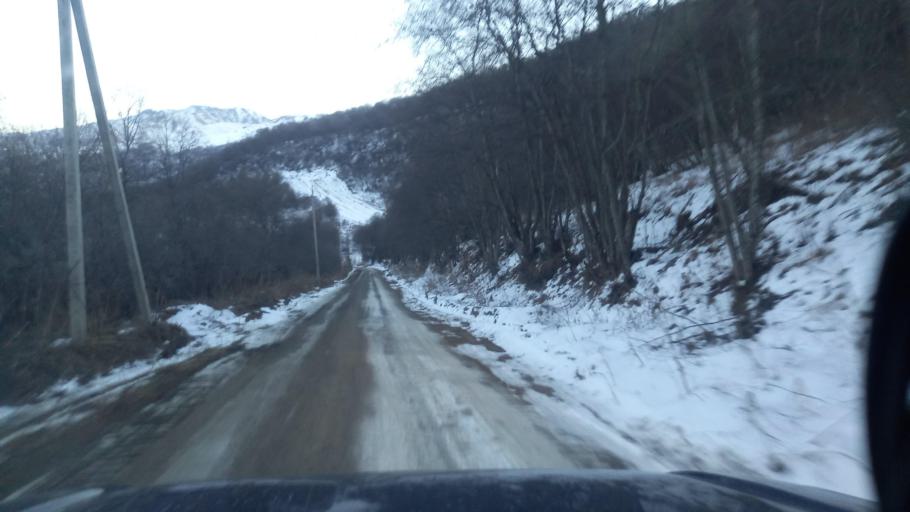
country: RU
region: Ingushetiya
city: Dzhayrakh
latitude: 42.8288
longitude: 44.5760
